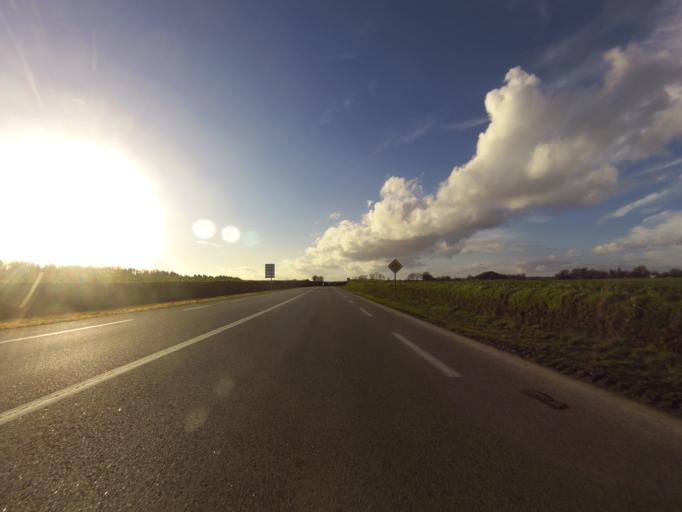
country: FR
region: Brittany
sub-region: Departement du Morbihan
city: Pleugriffet
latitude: 47.9793
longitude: -2.6929
